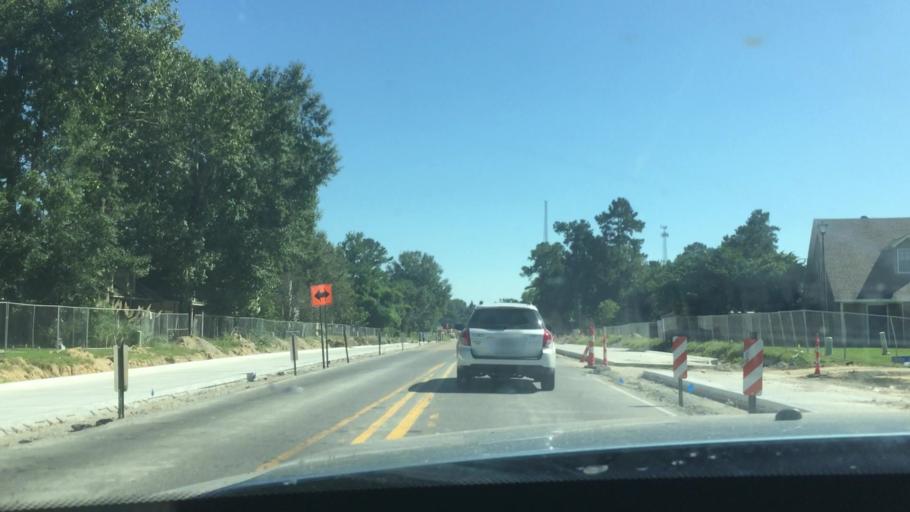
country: US
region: Louisiana
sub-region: East Baton Rouge Parish
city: Shenandoah
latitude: 30.4236
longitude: -91.0075
